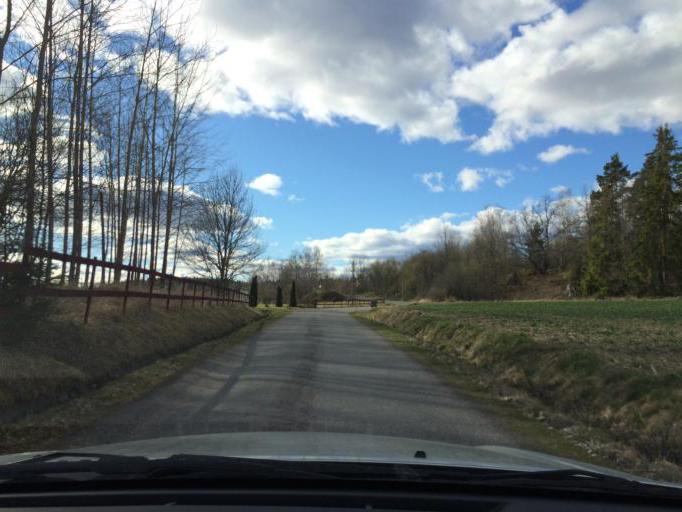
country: SE
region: Soedermanland
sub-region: Eskilstuna Kommun
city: Hallbybrunn
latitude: 59.4297
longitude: 16.3978
